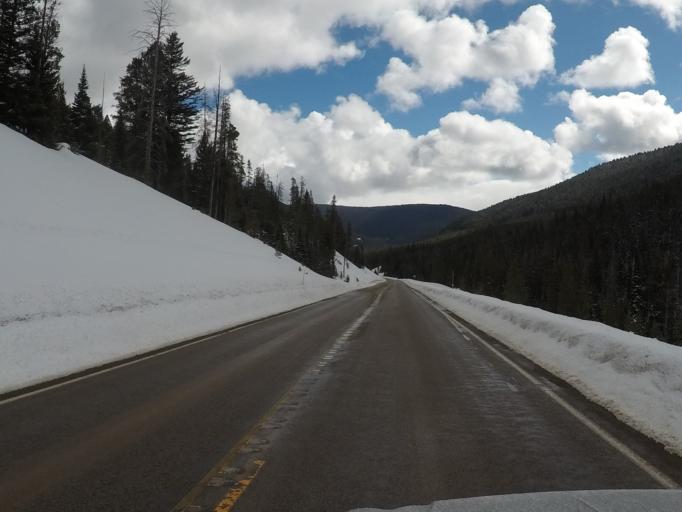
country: US
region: Montana
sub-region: Meagher County
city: White Sulphur Springs
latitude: 46.8063
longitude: -110.7061
